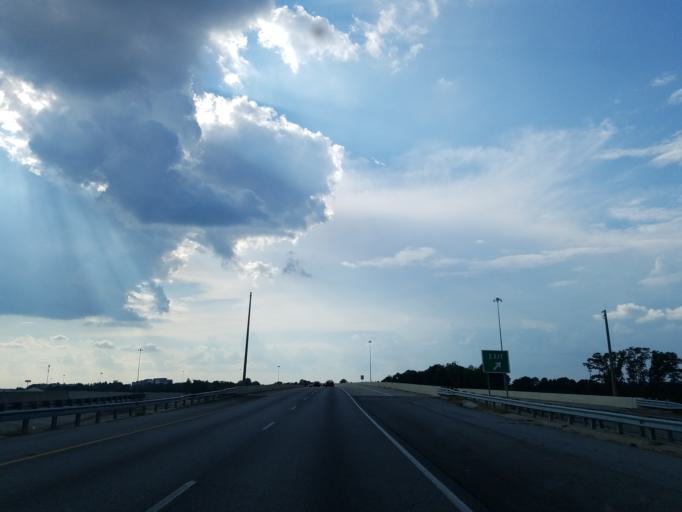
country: US
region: Georgia
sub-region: Gwinnett County
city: Duluth
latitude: 33.9647
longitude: -84.0978
